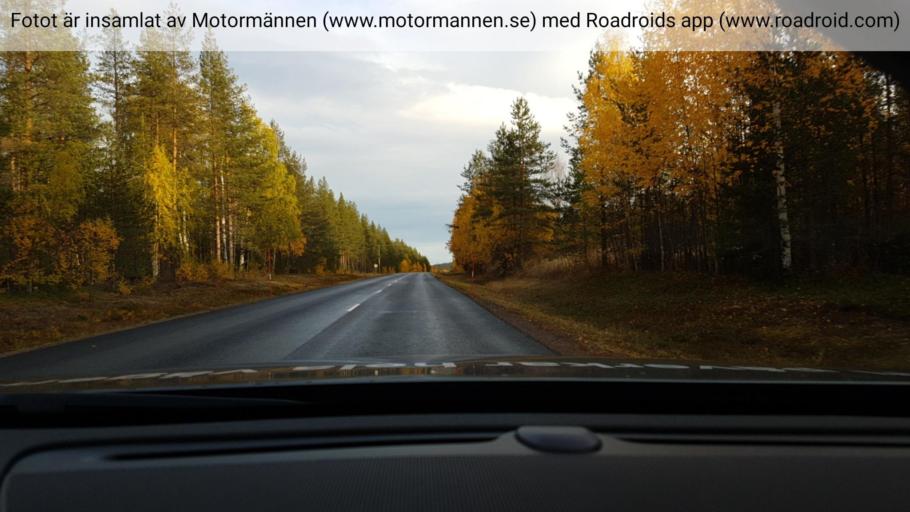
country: SE
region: Norrbotten
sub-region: Overkalix Kommun
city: OEverkalix
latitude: 66.9838
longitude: 22.6096
